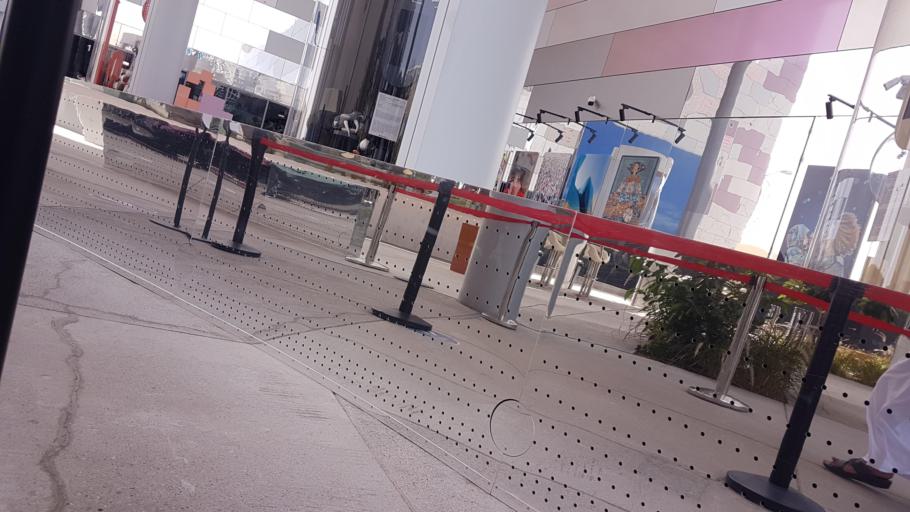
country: AE
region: Dubai
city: Dubai
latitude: 24.9568
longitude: 55.1482
